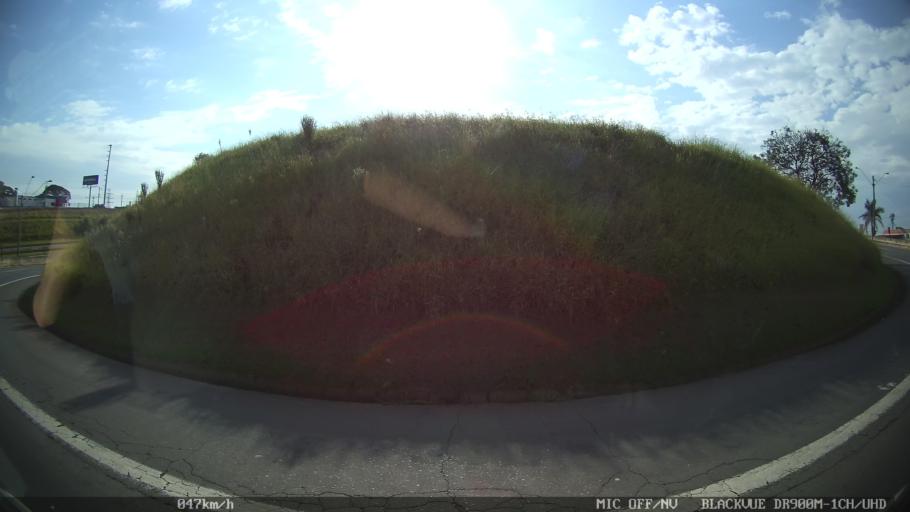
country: BR
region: Sao Paulo
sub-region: Paulinia
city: Paulinia
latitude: -22.7953
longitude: -47.1342
